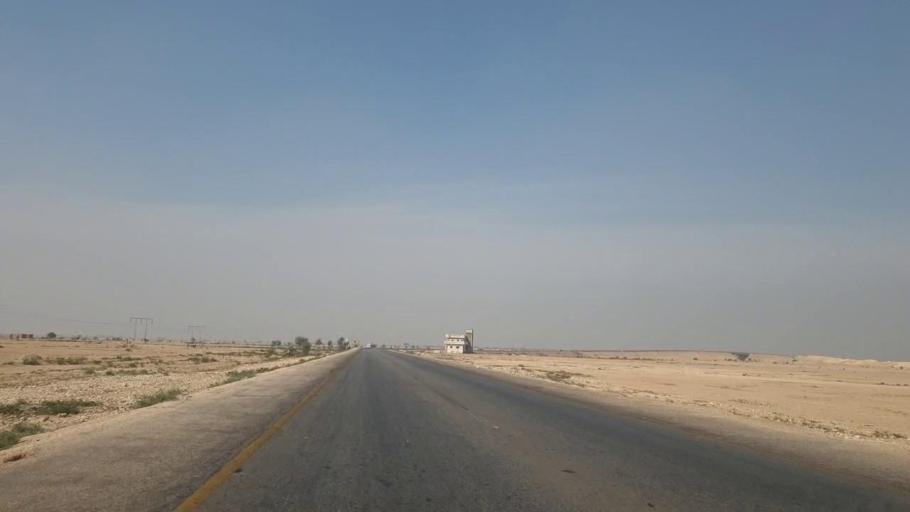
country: PK
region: Sindh
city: Hala
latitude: 25.8522
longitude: 68.2586
